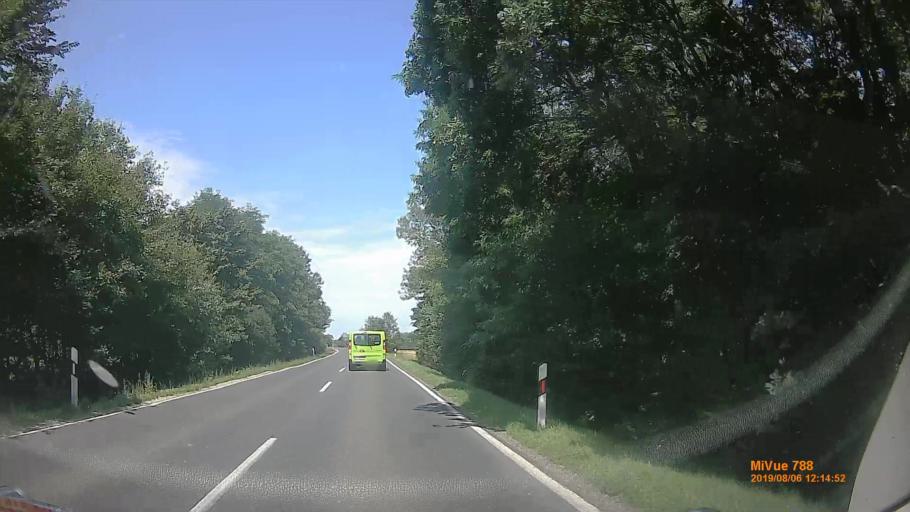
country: HU
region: Vas
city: Vasvar
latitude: 47.1441
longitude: 16.8262
